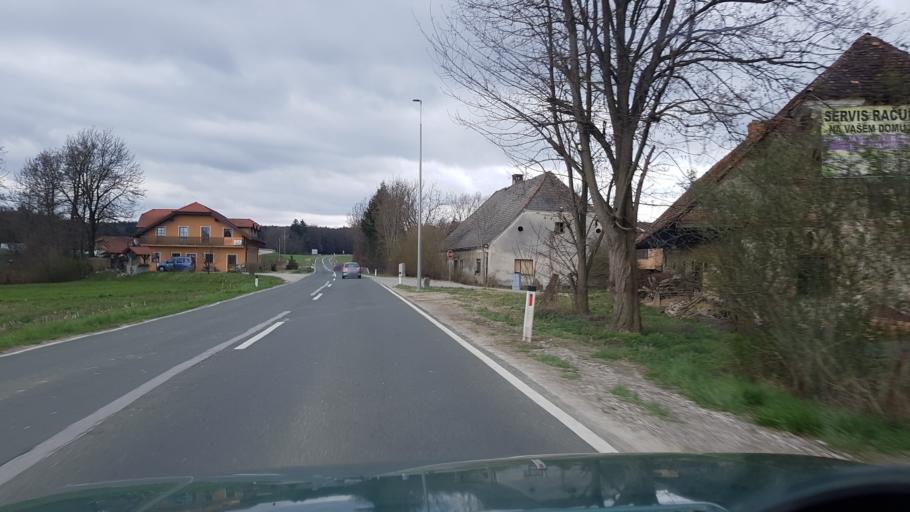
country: SI
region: Slovenska Bistrica
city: Slovenska Bistrica
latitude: 46.3769
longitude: 15.5497
